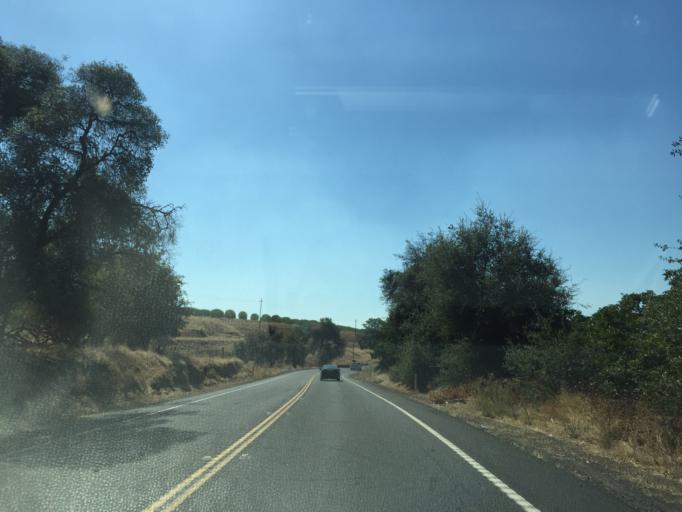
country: US
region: California
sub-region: Stanislaus County
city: East Oakdale
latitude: 37.7936
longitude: -120.7252
